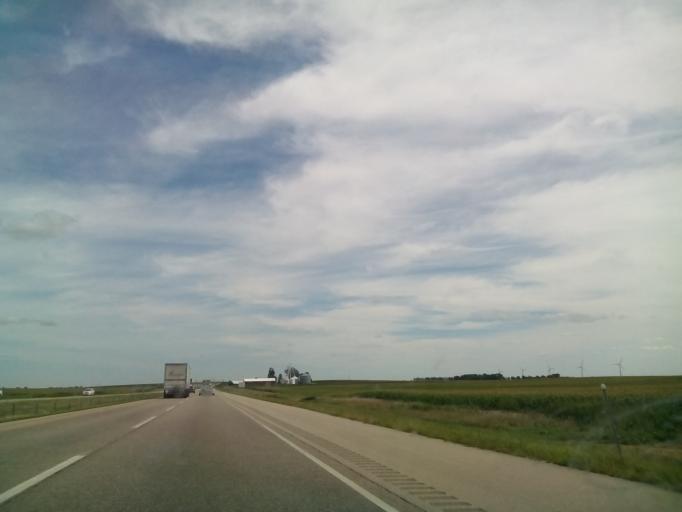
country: US
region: Illinois
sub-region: DeKalb County
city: Malta
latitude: 41.8995
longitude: -88.8967
